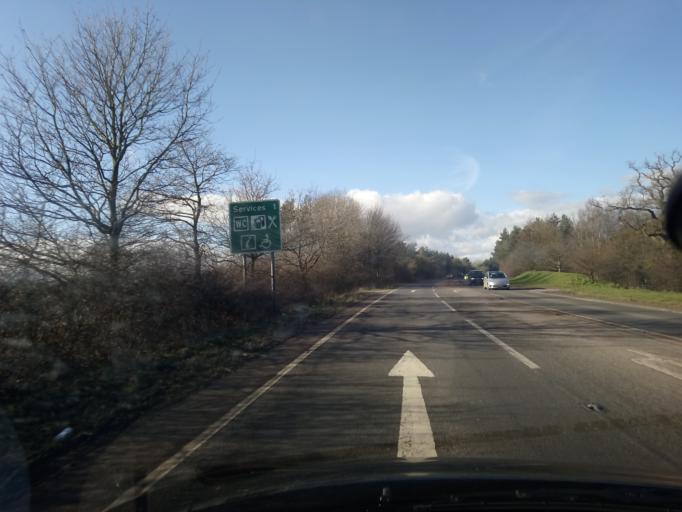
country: GB
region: England
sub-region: Shropshire
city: Whitchurch
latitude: 52.9569
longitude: -2.6906
